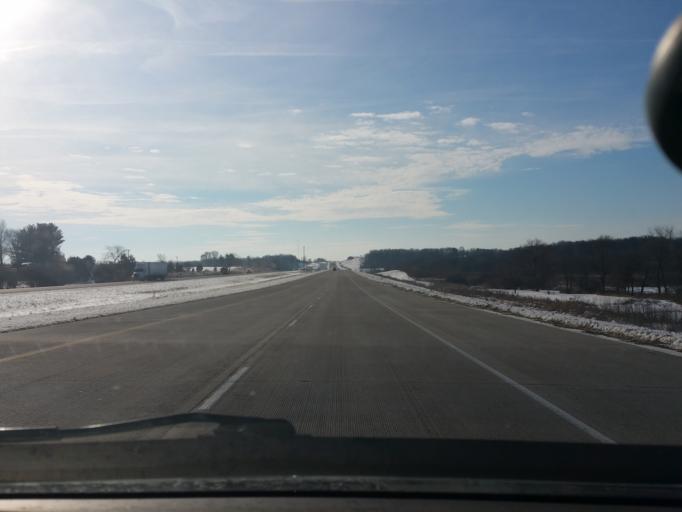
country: US
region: Iowa
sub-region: Warren County
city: Norwalk
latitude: 41.4675
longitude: -93.7804
